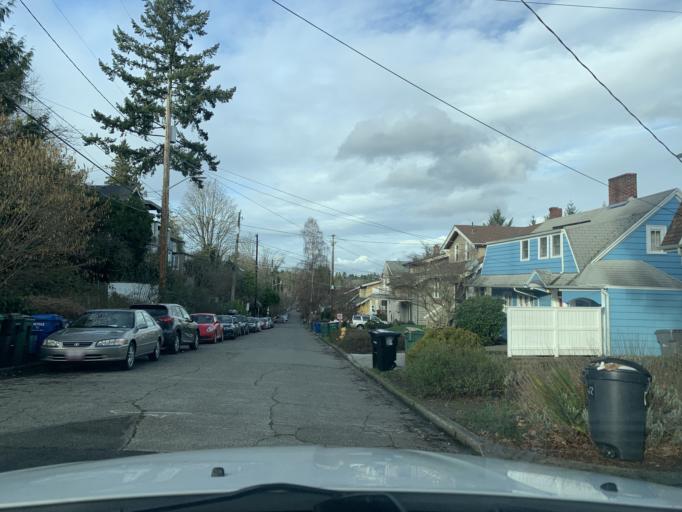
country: US
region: Washington
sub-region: King County
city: Seattle
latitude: 47.6655
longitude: -122.3055
